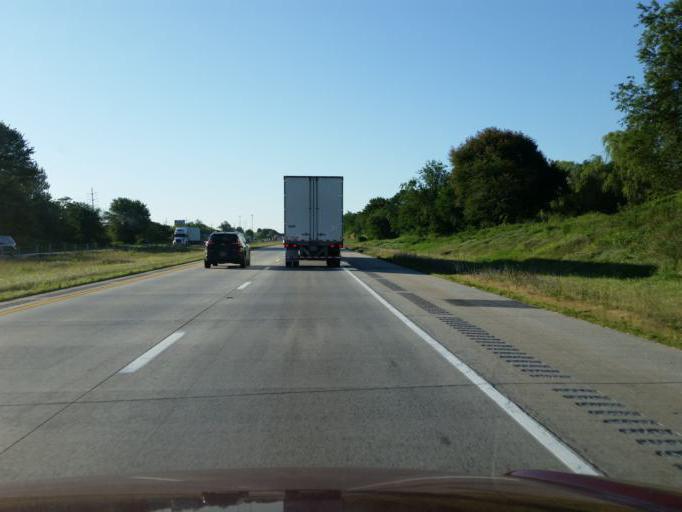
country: US
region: Pennsylvania
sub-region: Lancaster County
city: Elizabethtown
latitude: 40.1622
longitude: -76.5805
